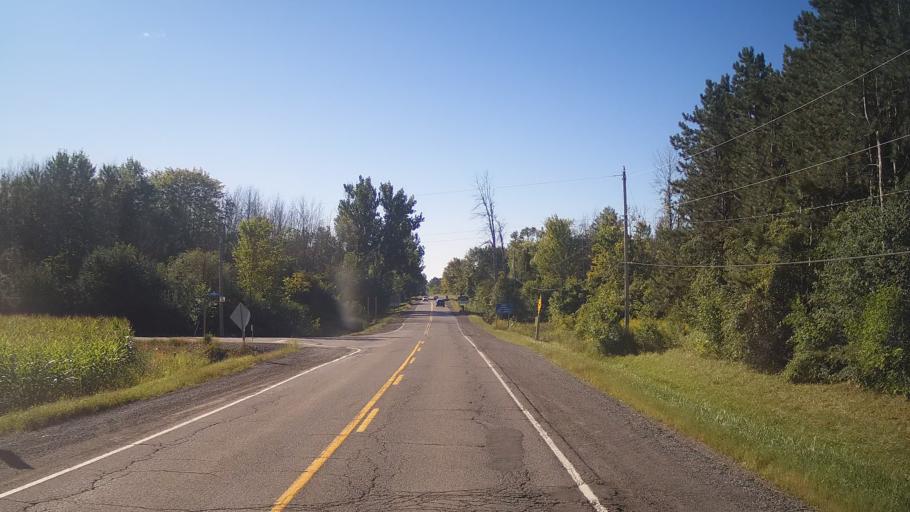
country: CA
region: Ontario
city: Bells Corners
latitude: 45.1099
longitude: -75.6162
